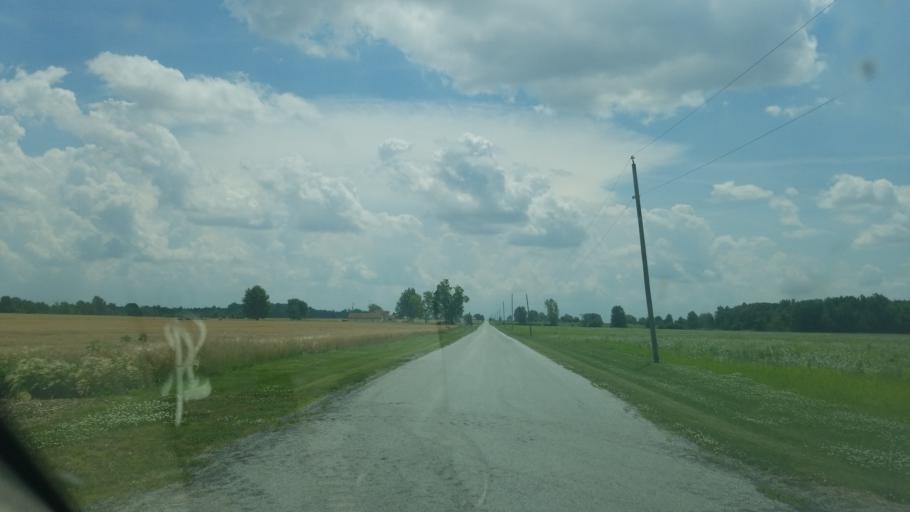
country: US
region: Ohio
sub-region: Hancock County
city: Arlington
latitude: 40.8156
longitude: -83.6050
